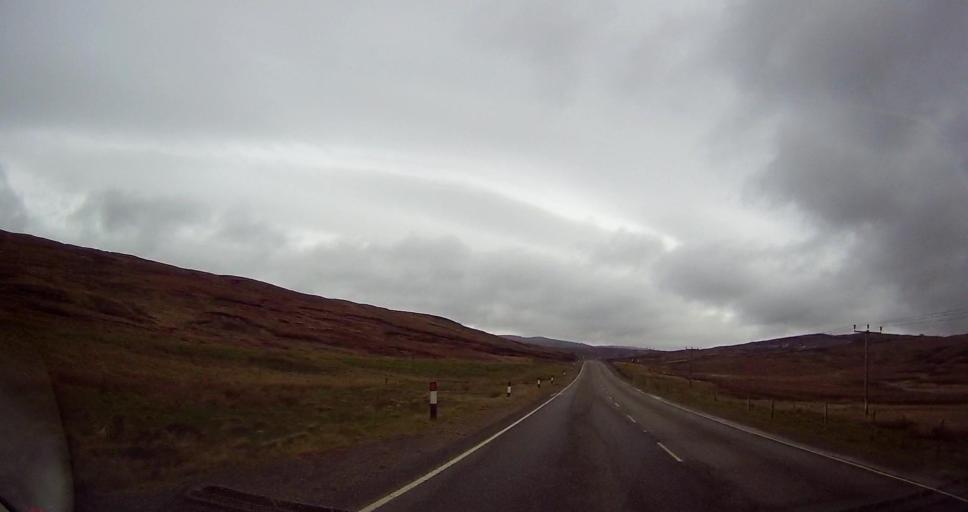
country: GB
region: Scotland
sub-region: Shetland Islands
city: Lerwick
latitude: 60.2683
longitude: -1.2316
